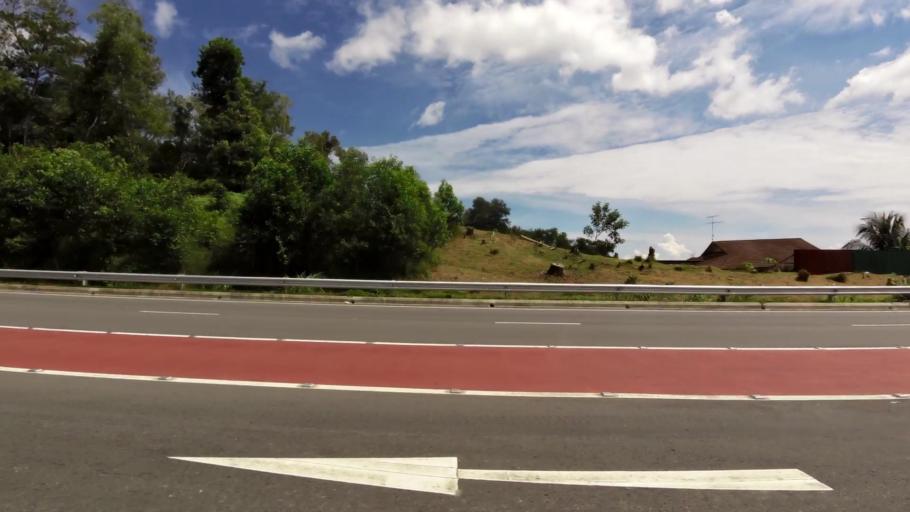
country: BN
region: Brunei and Muara
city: Bandar Seri Begawan
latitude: 4.9329
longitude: 114.8929
